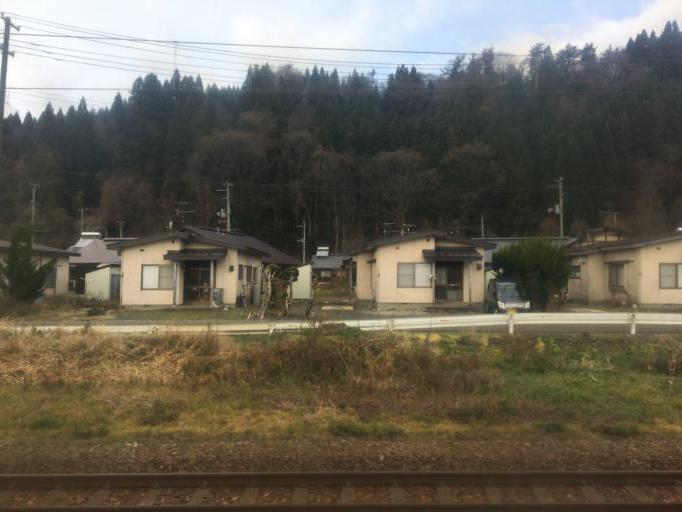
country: JP
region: Akita
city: Takanosu
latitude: 40.2110
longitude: 140.2340
